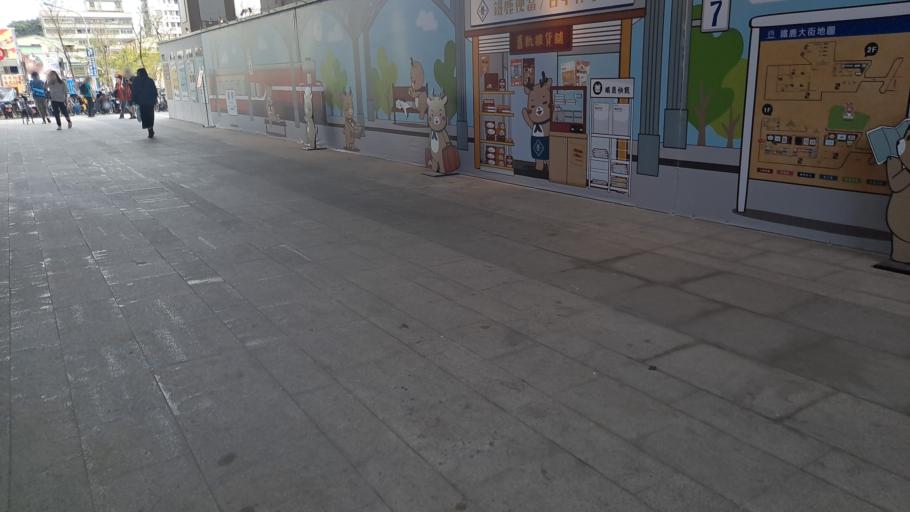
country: TW
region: Taiwan
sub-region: Taichung City
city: Taichung
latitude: 24.1365
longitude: 120.6863
